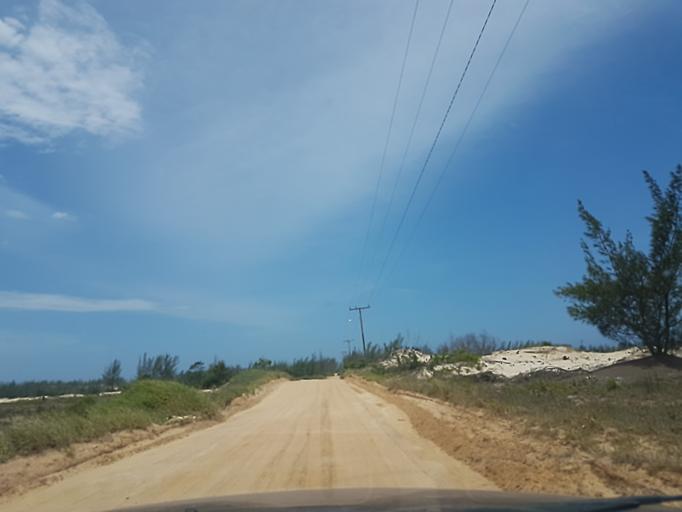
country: BR
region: Santa Catarina
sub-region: Jaguaruna
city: Jaguaruna
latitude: -28.6545
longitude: -48.9567
